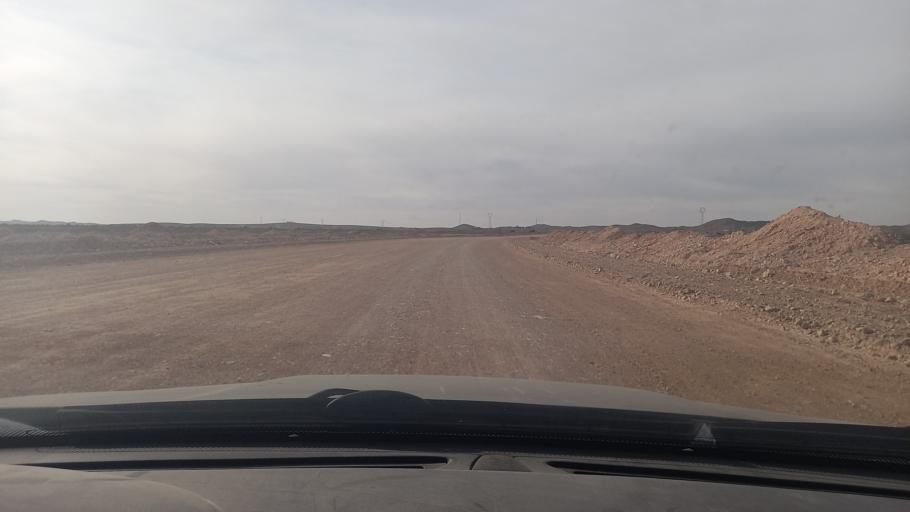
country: TN
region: Tataouine
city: Tataouine
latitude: 33.1362
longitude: 10.5048
